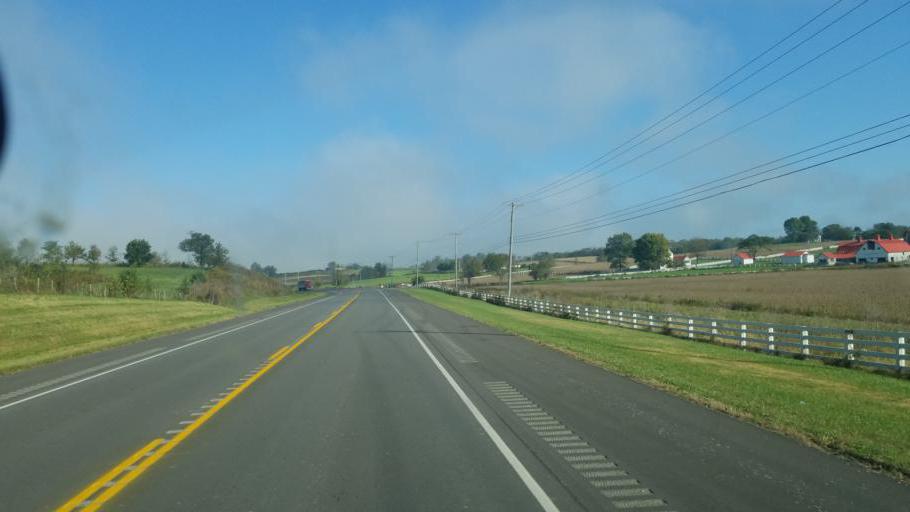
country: US
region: Kentucky
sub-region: Fleming County
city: Flemingsburg
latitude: 38.4756
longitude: -83.7566
